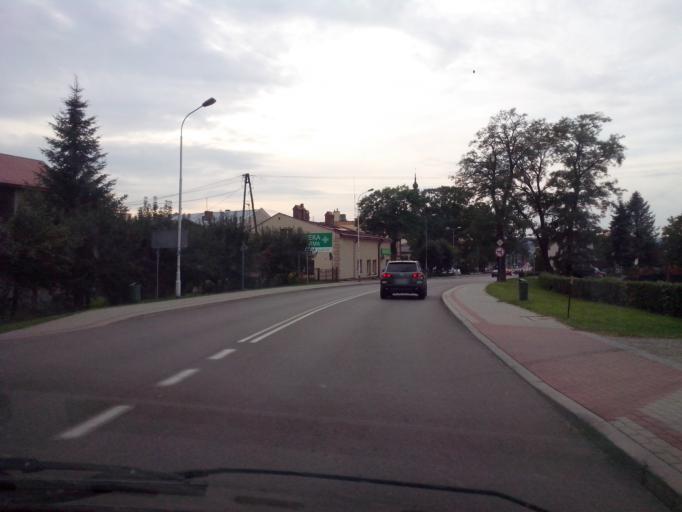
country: PL
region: Subcarpathian Voivodeship
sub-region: Powiat przemyski
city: Dubiecko
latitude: 49.8240
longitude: 22.3949
